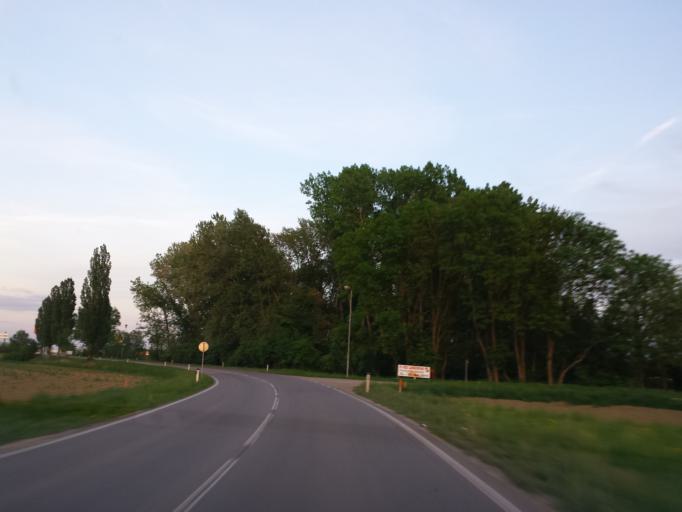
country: AT
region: Lower Austria
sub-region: Politischer Bezirk Tulln
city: Langenrohr
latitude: 48.3189
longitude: 16.0125
